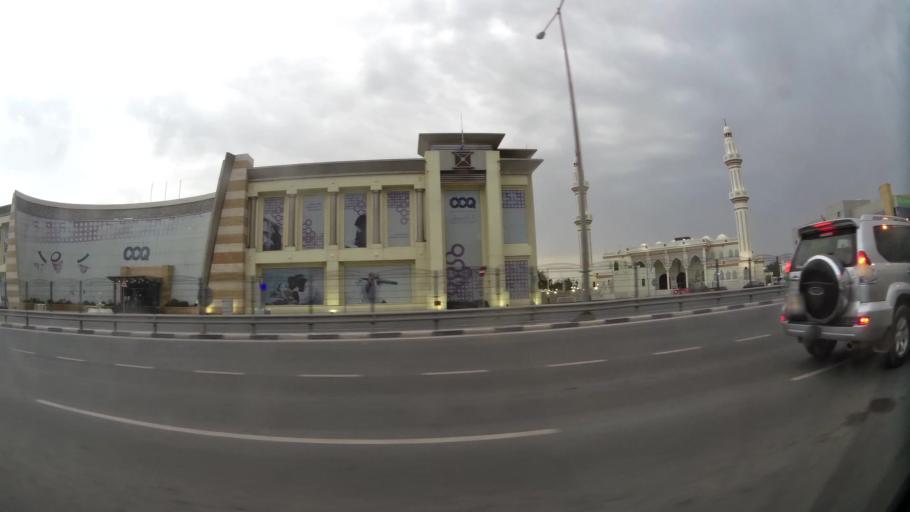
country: QA
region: Baladiyat ad Dawhah
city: Doha
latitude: 25.2663
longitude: 51.5161
